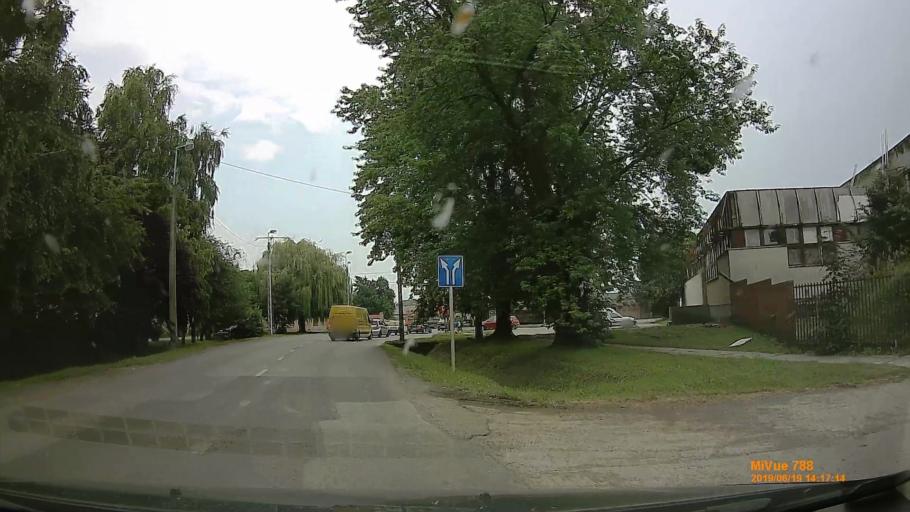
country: HU
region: Baranya
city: Szigetvar
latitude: 46.0491
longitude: 17.7849
